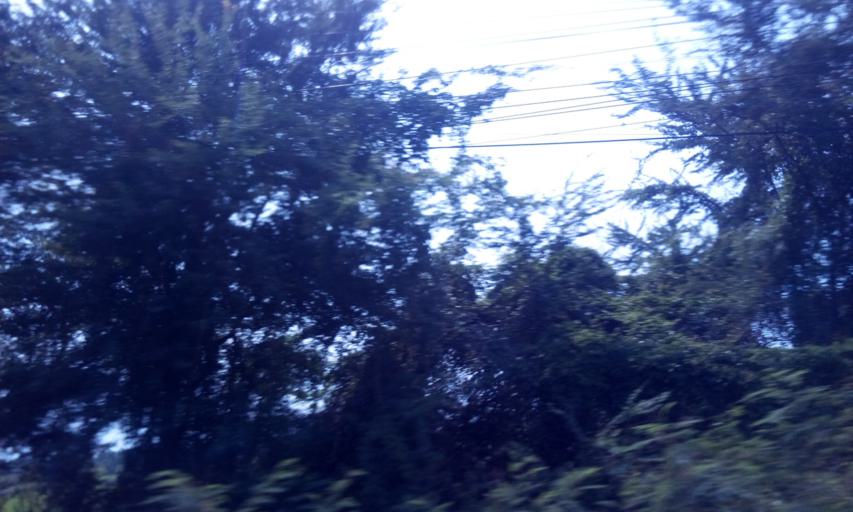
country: TH
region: Nonthaburi
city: Sai Noi
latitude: 13.9369
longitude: 100.3166
